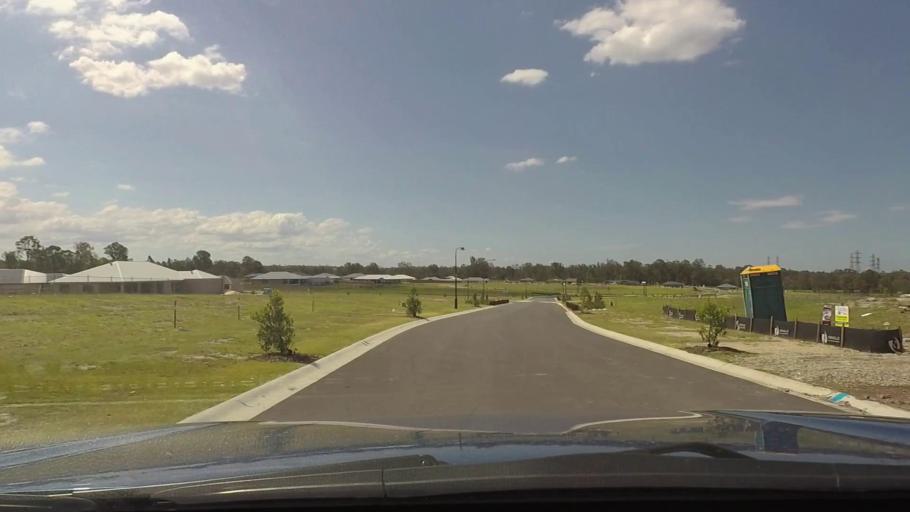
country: AU
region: Queensland
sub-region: Logan
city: North Maclean
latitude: -27.7398
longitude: 152.9509
